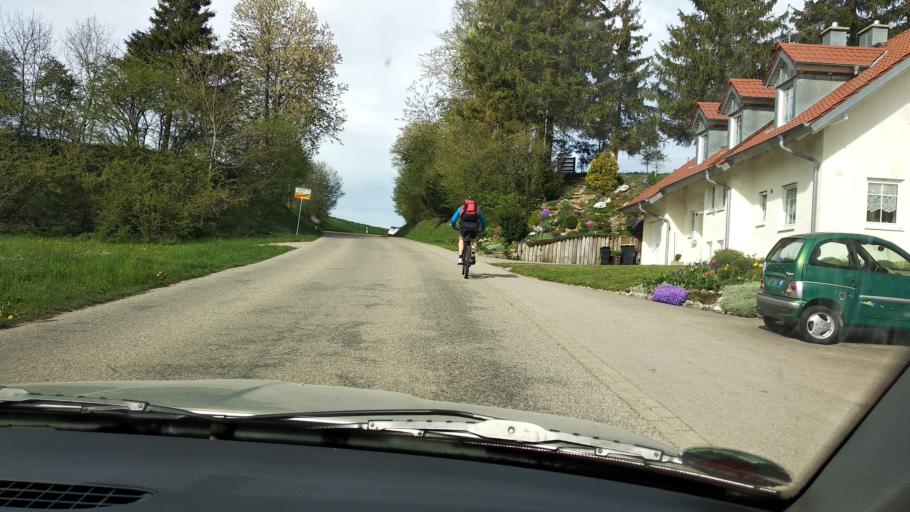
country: DE
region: Bavaria
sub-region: Swabia
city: Lachen
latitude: 47.9301
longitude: 10.2295
